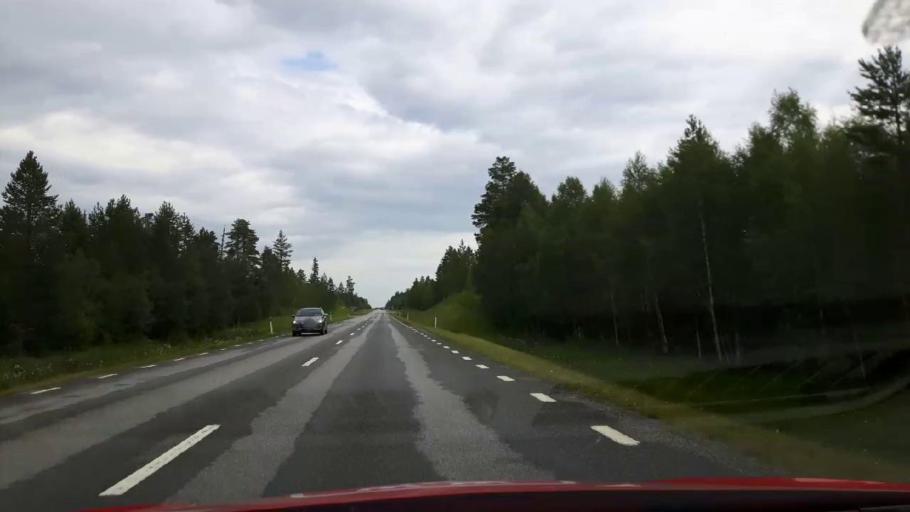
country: SE
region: Jaemtland
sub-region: Stroemsunds Kommun
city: Stroemsund
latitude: 63.6923
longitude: 15.4234
